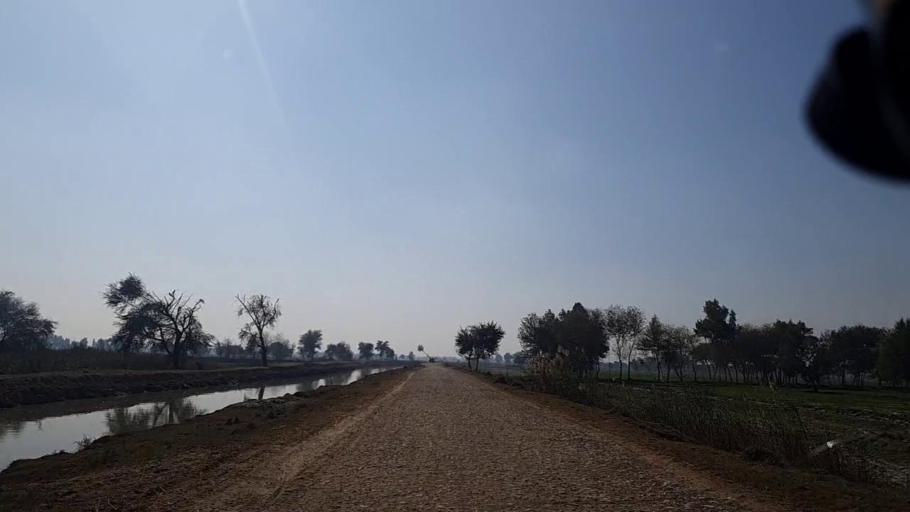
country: PK
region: Sindh
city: Khanpur
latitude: 27.8012
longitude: 69.4100
